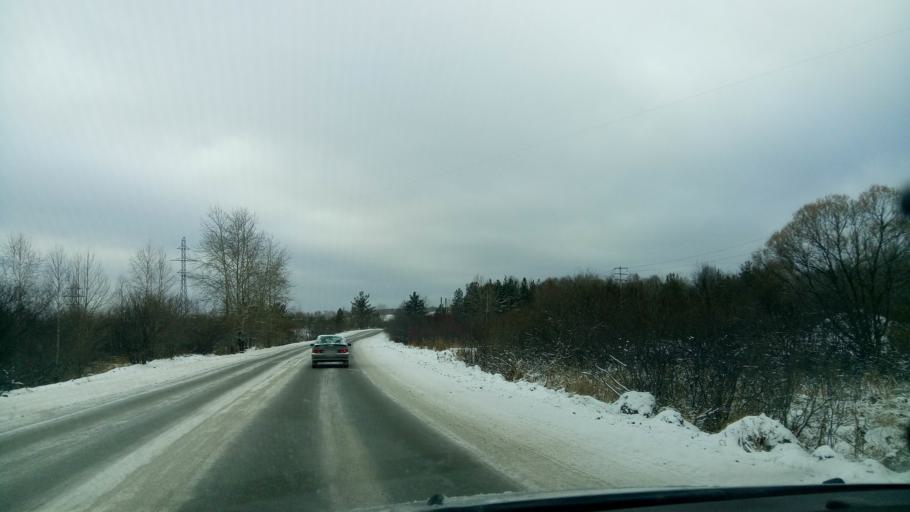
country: RU
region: Sverdlovsk
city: Polevskoy
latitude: 56.4564
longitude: 60.1924
